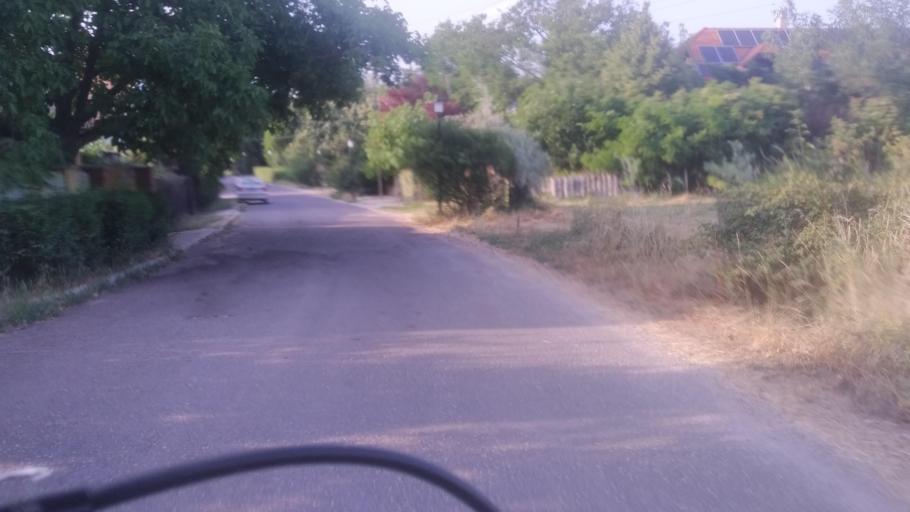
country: HU
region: Pest
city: Urom
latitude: 47.5929
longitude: 19.0212
